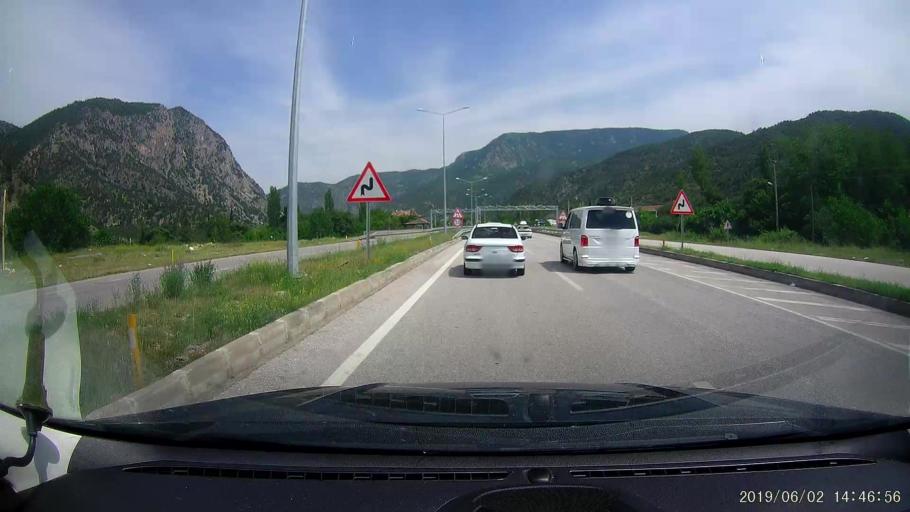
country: TR
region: Corum
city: Hacihamza
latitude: 41.0724
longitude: 34.4563
